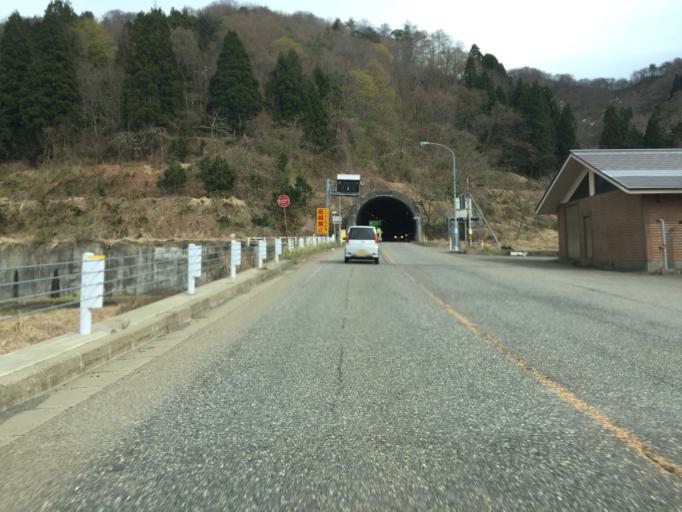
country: JP
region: Niigata
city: Nagaoka
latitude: 37.4557
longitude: 138.9224
